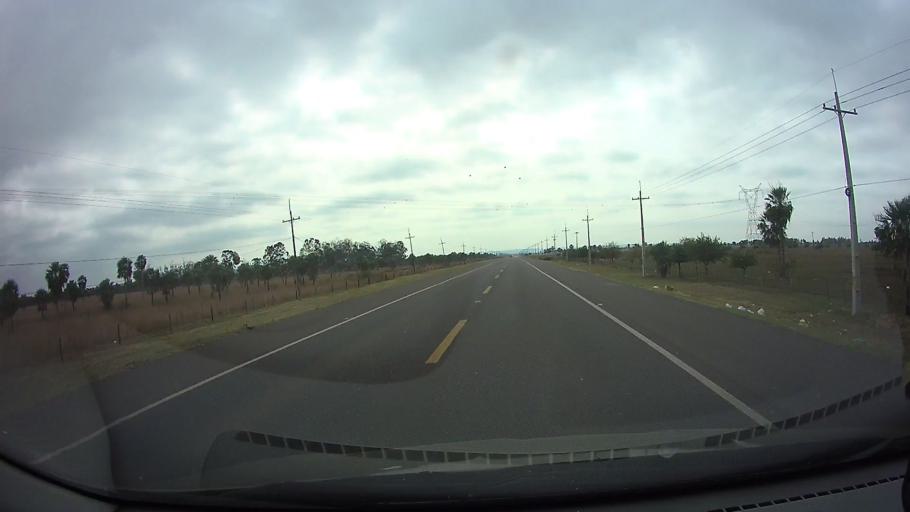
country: PY
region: Cordillera
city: Emboscada
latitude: -25.0850
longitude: -57.2837
